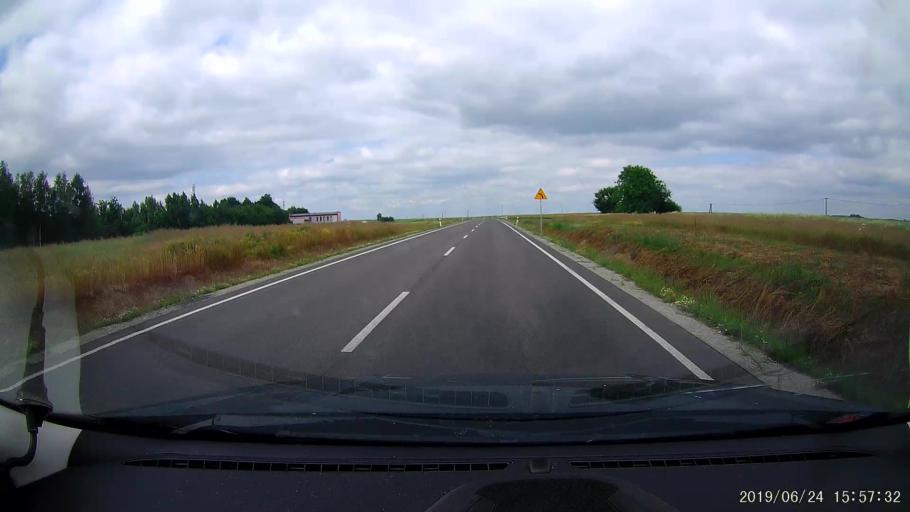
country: PL
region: Subcarpathian Voivodeship
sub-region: Powiat lubaczowski
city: Cieszanow
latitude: 50.2480
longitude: 23.1389
